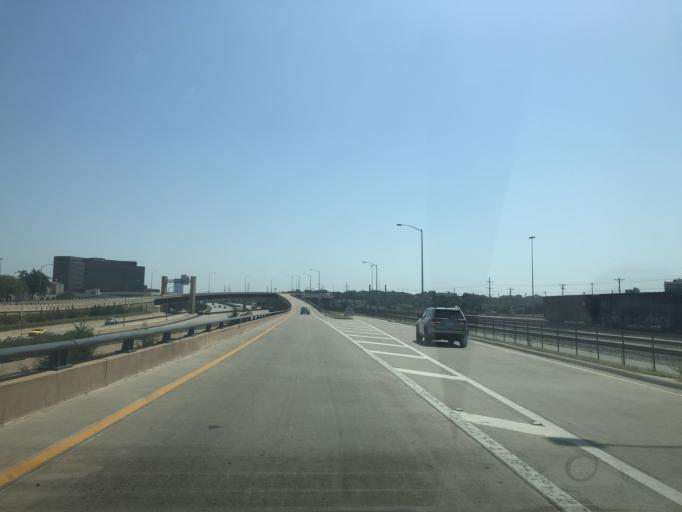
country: US
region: Texas
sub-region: Tarrant County
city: Fort Worth
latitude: 32.7293
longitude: -97.3682
